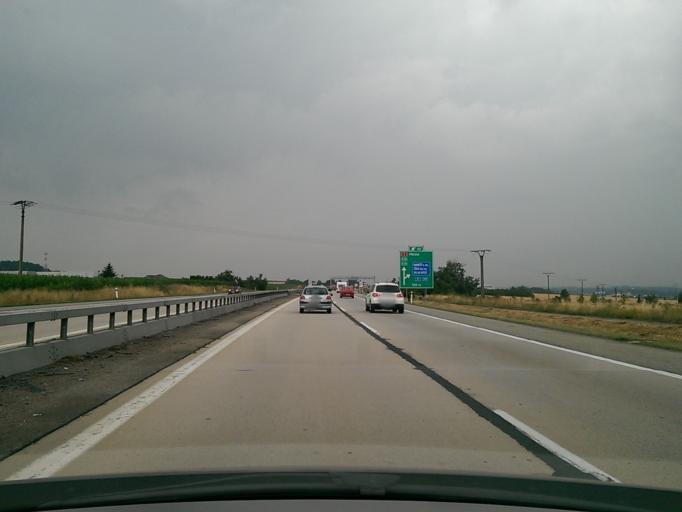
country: CZ
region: Vysocina
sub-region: Okres Zd'ar nad Sazavou
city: Velka Bites
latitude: 49.2726
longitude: 16.2387
